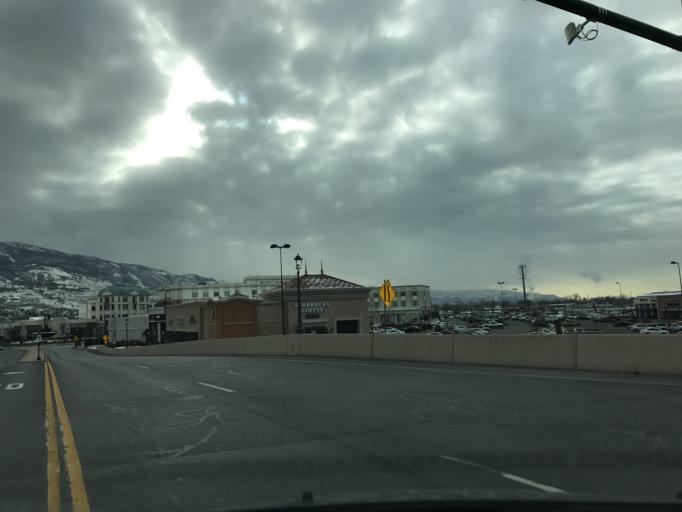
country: US
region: Utah
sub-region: Davis County
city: Farmington
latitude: 40.9865
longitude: -111.9089
